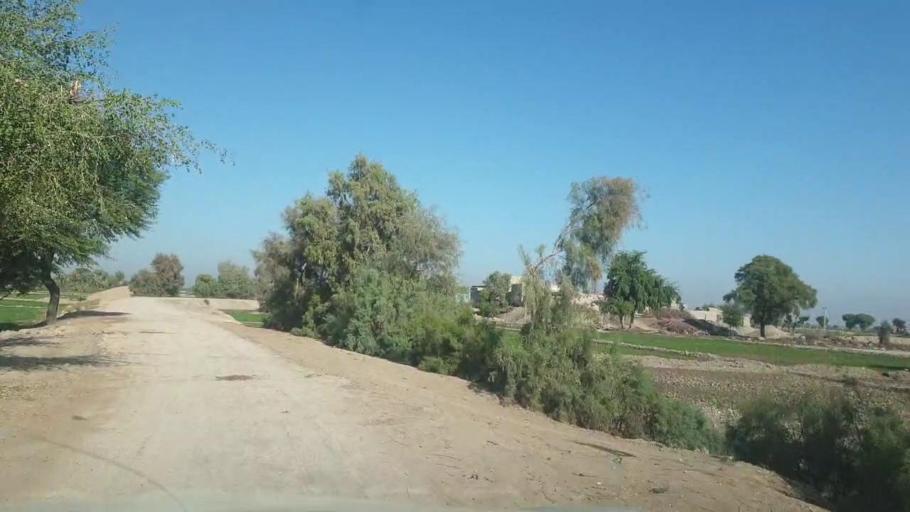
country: PK
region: Sindh
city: Bhan
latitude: 26.5237
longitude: 67.6426
